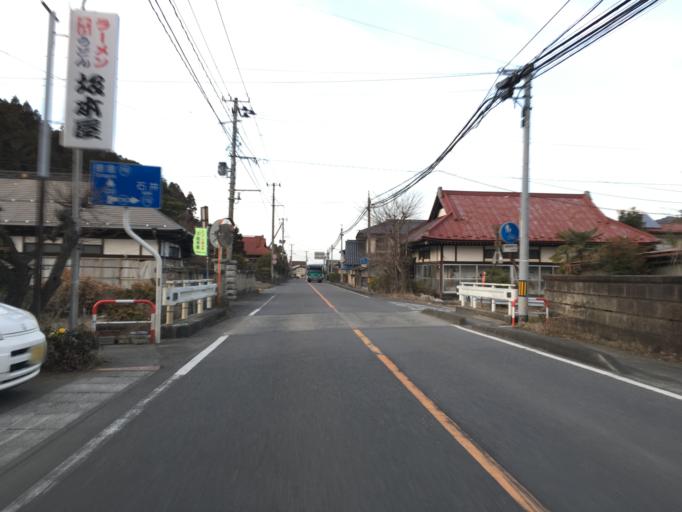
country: JP
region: Ibaraki
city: Daigo
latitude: 36.9058
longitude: 140.4071
